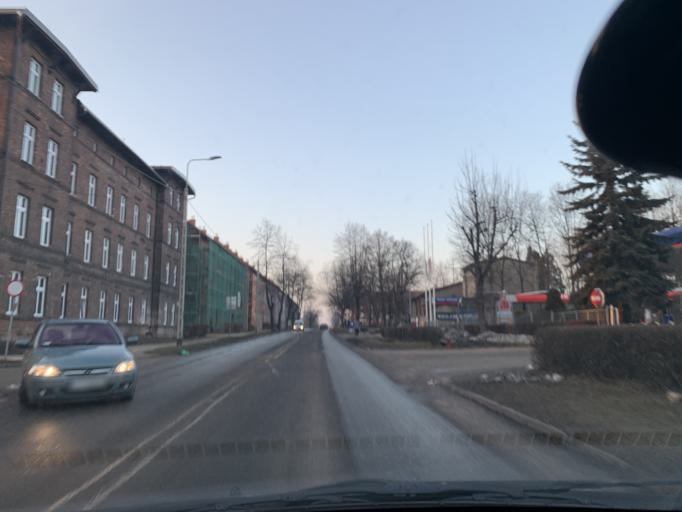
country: PL
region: Silesian Voivodeship
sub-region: Powiat tarnogorski
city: Radzionkow
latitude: 50.3858
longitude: 18.8997
